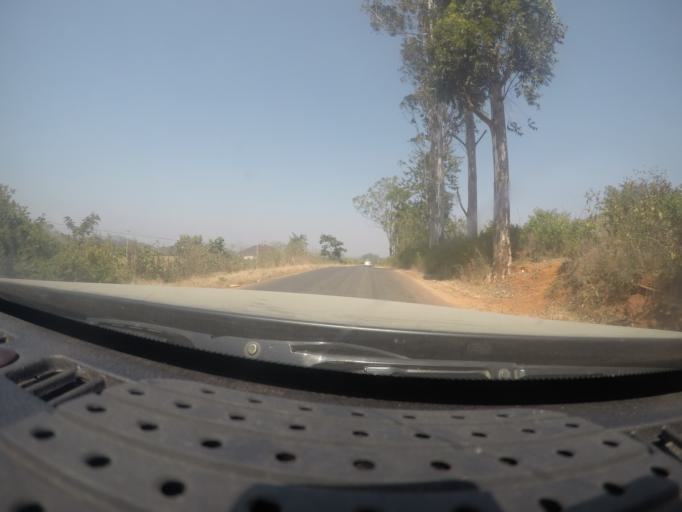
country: MM
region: Shan
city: Taunggyi
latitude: 20.9096
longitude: 96.5695
